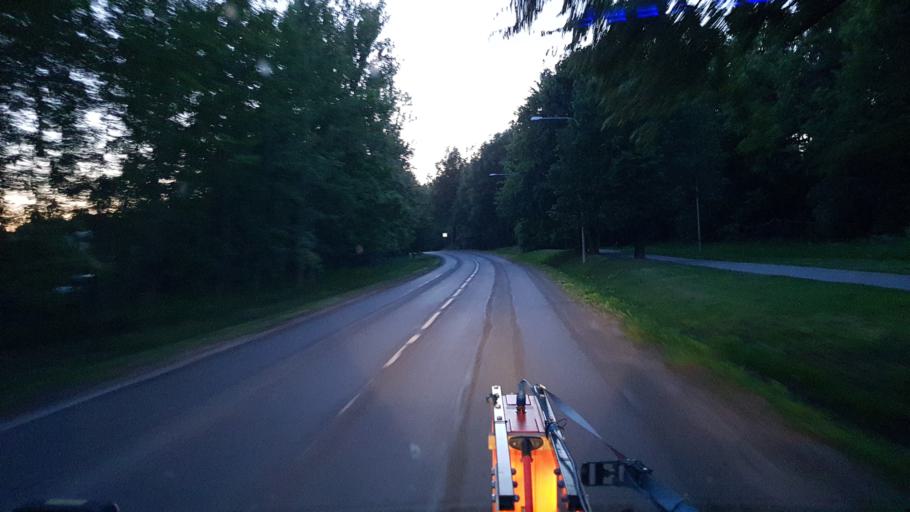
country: EE
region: Harju
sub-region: Saue vald
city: Laagri
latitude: 59.4334
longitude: 24.6198
